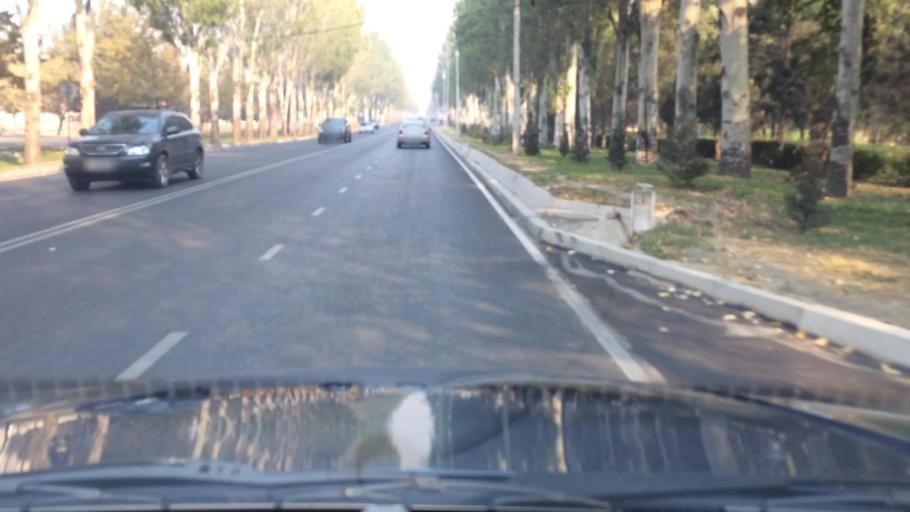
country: KG
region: Chuy
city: Bishkek
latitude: 42.8303
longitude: 74.5853
